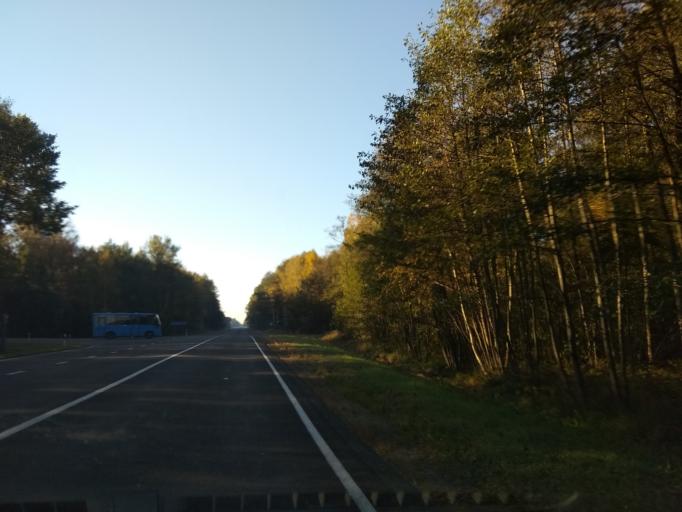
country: BY
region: Brest
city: Kobryn
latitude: 52.0610
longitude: 24.2823
